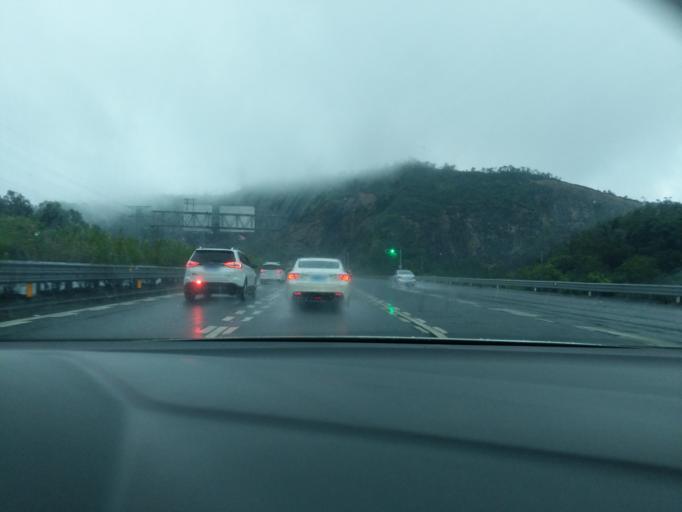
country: CN
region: Guangdong
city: Duruan
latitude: 22.5840
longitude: 113.0326
